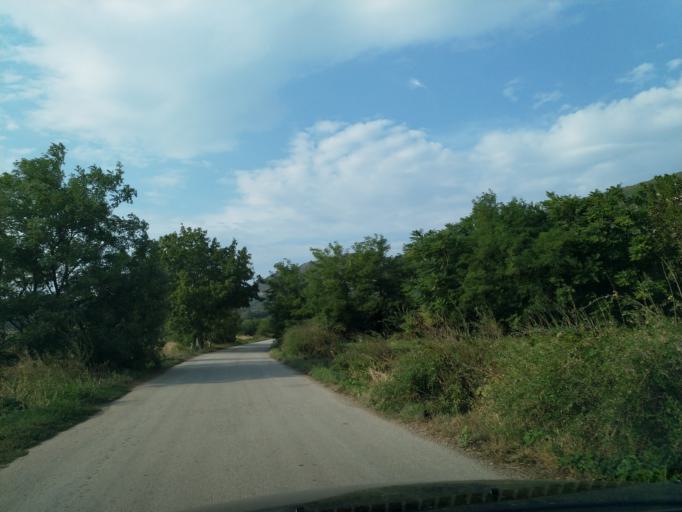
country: RS
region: Central Serbia
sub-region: Pomoravski Okrug
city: Paracin
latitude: 43.8268
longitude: 21.5419
